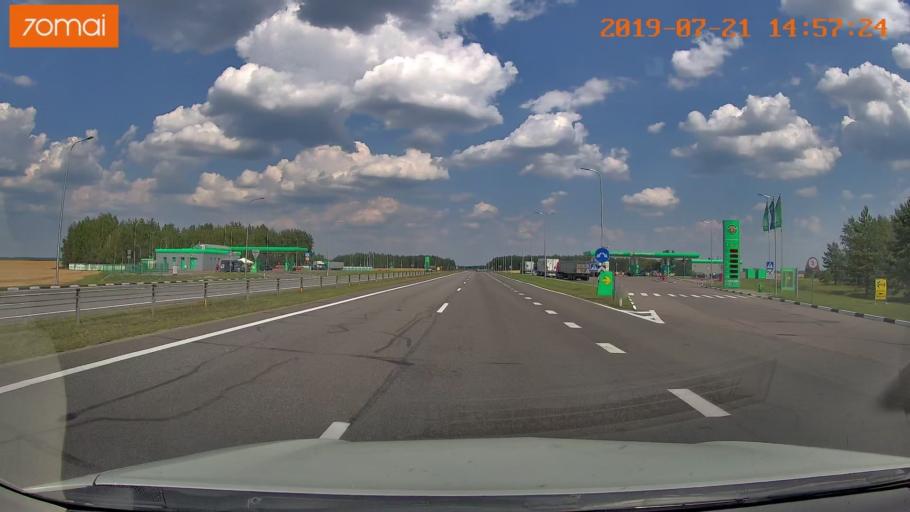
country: BY
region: Minsk
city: Stowbtsy
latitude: 53.5328
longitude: 26.7630
